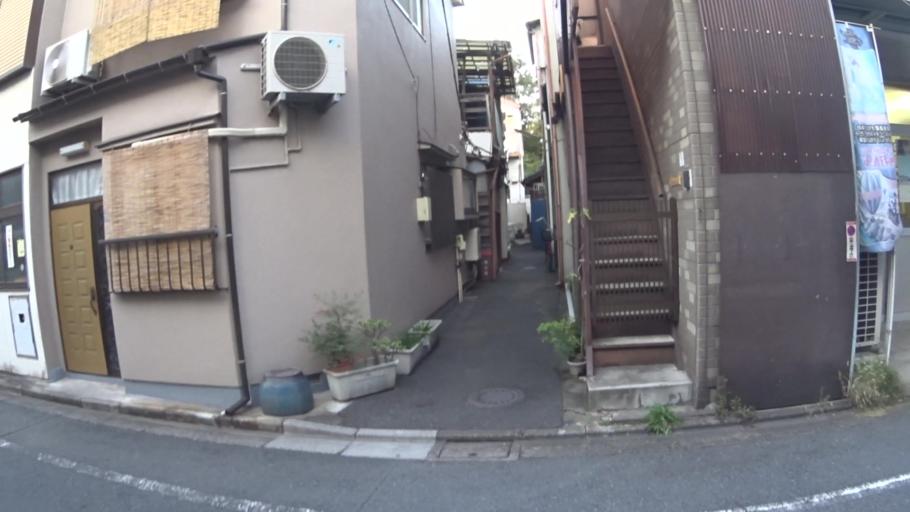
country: JP
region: Tokyo
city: Tokyo
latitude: 35.7199
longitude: 139.7655
